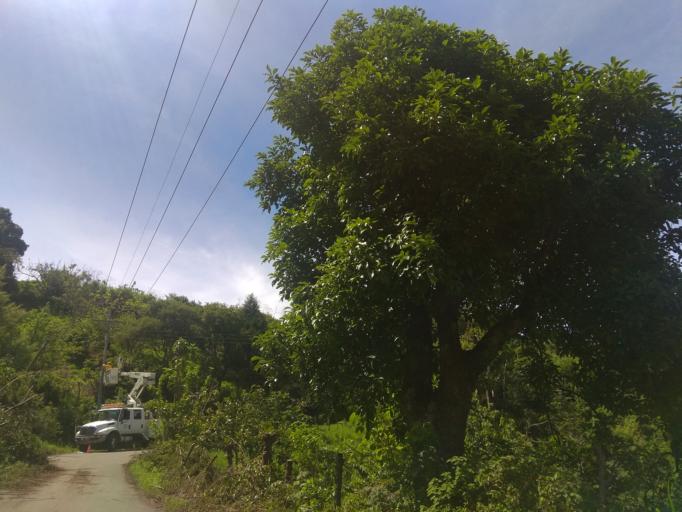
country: CR
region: Cartago
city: Cot
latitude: 9.9223
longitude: -83.9010
